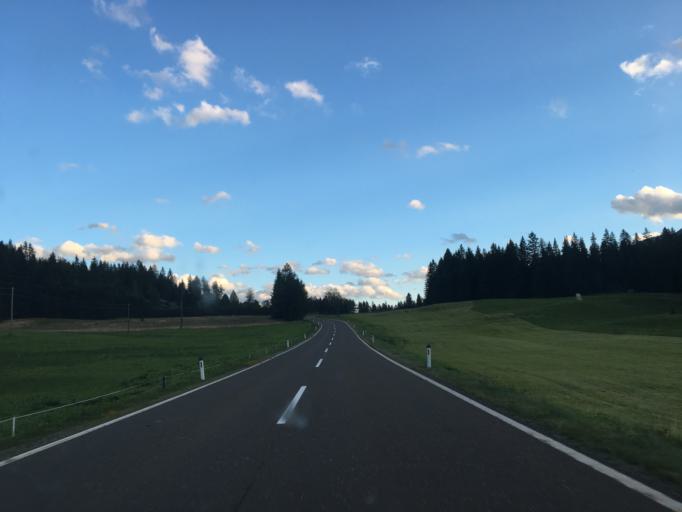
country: AT
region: Styria
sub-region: Politischer Bezirk Murtal
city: Hohentauern
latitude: 47.4153
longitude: 14.4627
